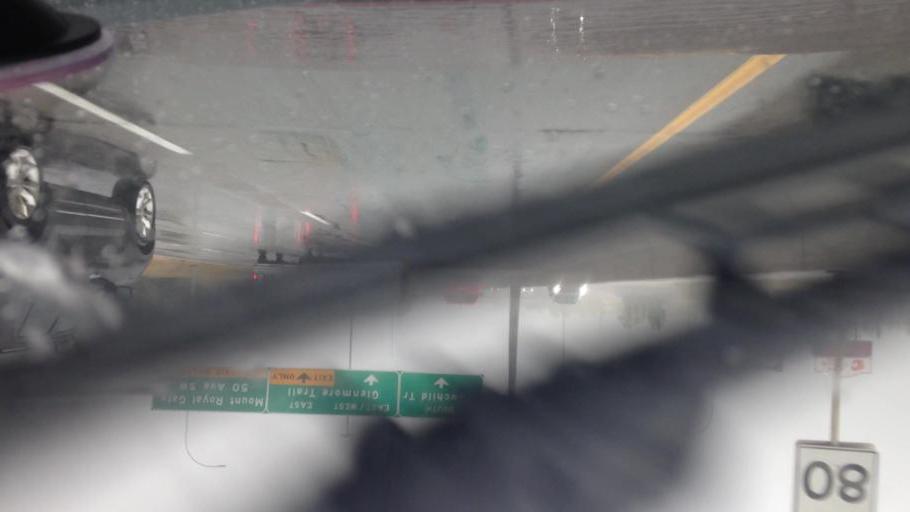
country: CA
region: Alberta
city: Calgary
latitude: 51.0120
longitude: -114.1181
